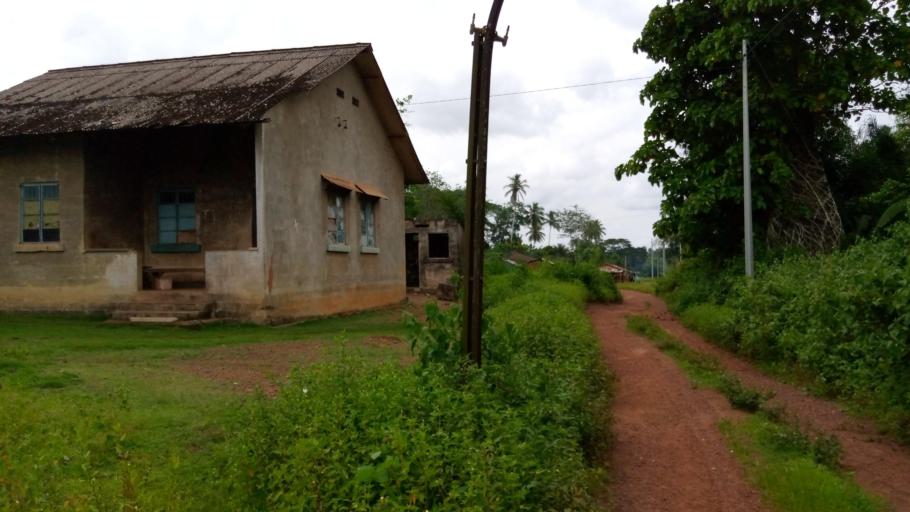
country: SL
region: Southern Province
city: Rotifunk
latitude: 8.1896
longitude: -12.5665
